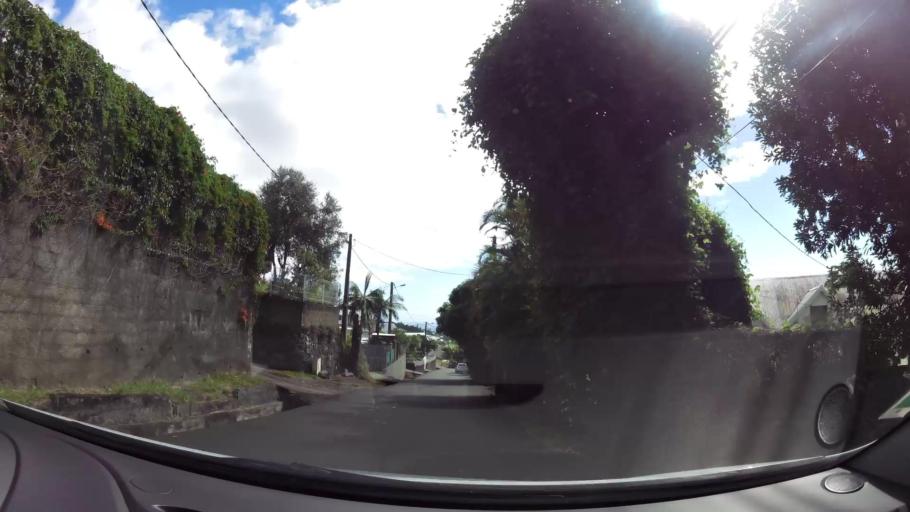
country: RE
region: Reunion
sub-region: Reunion
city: Saint-Denis
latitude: -20.9296
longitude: 55.4898
